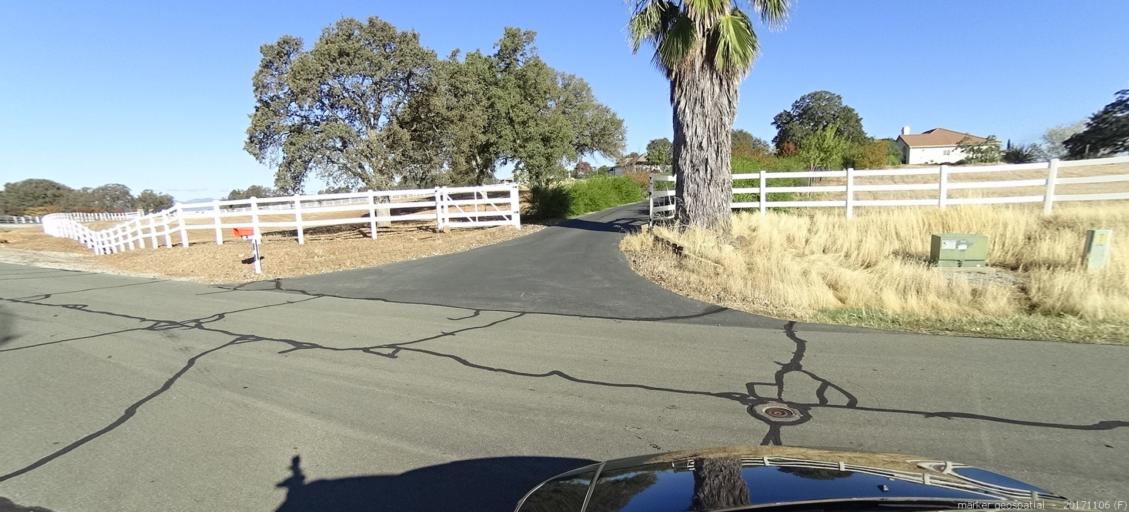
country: US
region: California
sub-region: Shasta County
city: Palo Cedro
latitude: 40.5029
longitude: -122.2443
